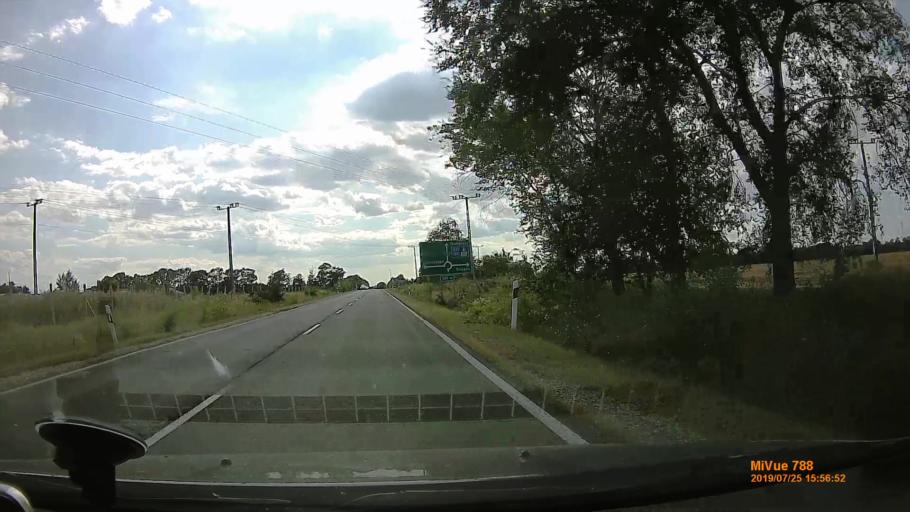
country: HU
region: Borsod-Abauj-Zemplen
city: Mezokovesd
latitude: 47.8232
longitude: 20.5748
